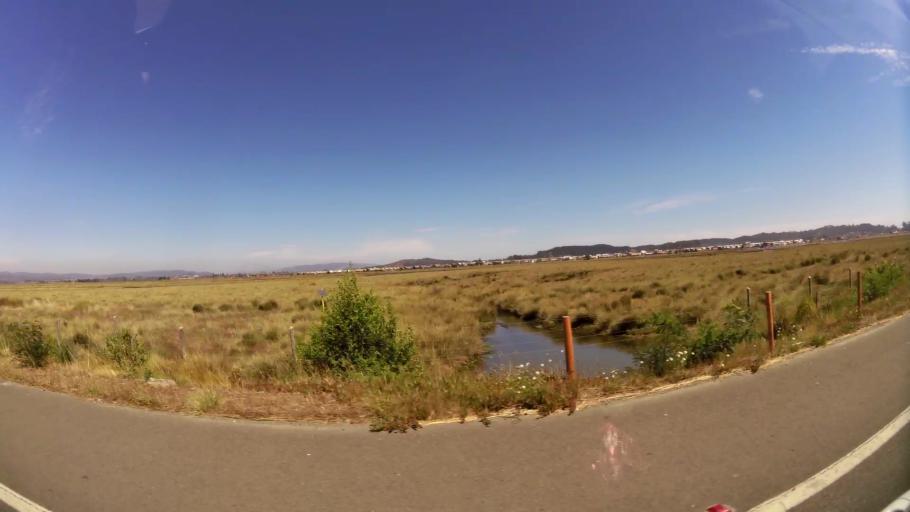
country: CL
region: Biobio
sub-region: Provincia de Concepcion
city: Talcahuano
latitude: -36.7335
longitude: -73.0842
